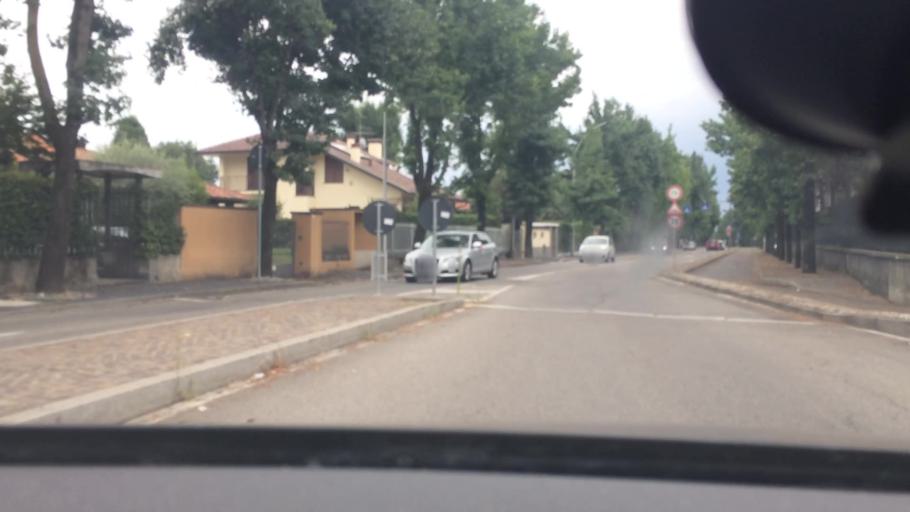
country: IT
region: Lombardy
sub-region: Citta metropolitana di Milano
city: Cerro Maggiore
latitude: 45.5942
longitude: 8.9576
